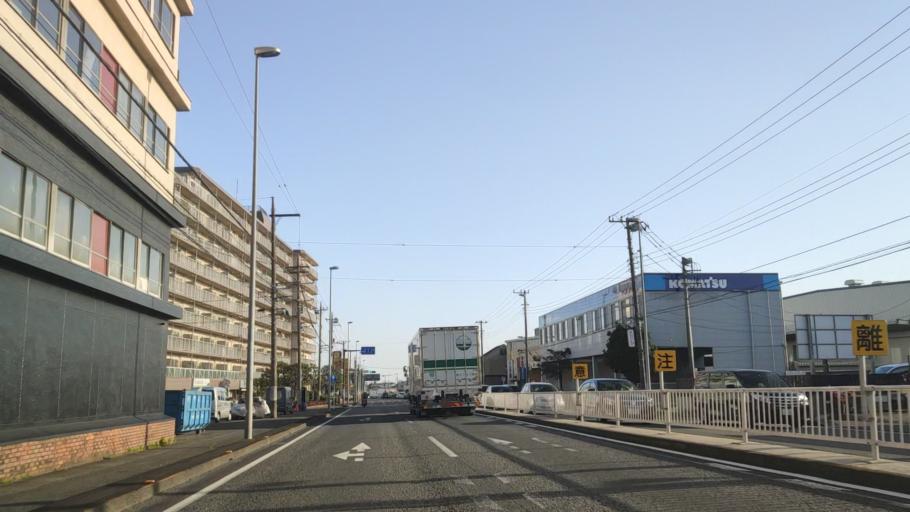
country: JP
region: Kanagawa
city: Zama
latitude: 35.4804
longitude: 139.3660
